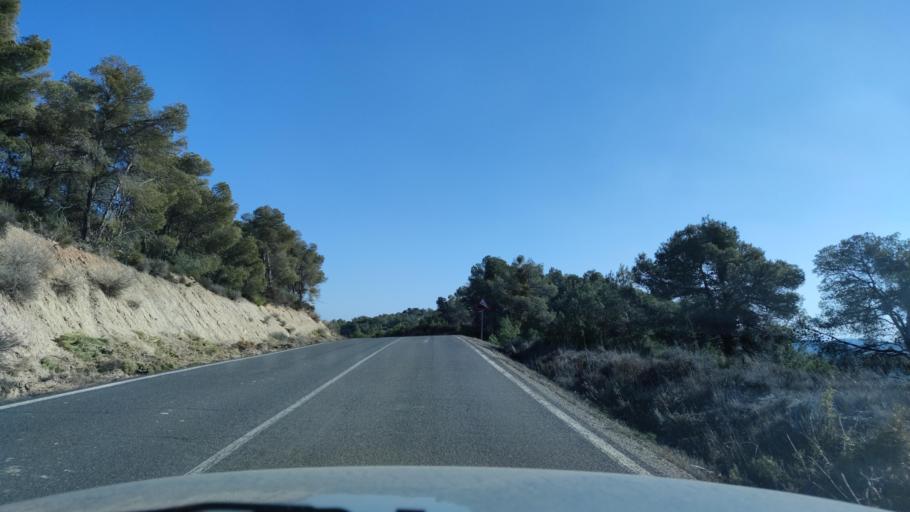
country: ES
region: Catalonia
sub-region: Provincia de Lleida
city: Maials
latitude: 41.3297
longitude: 0.4342
